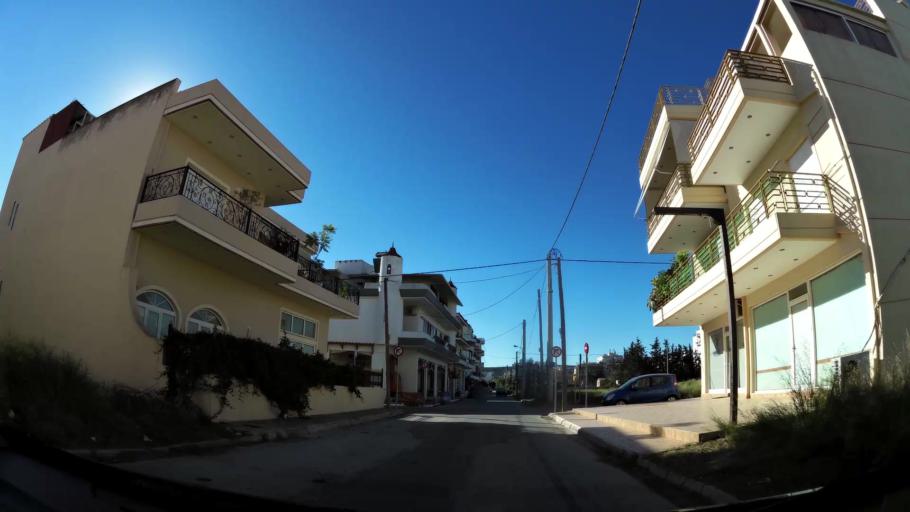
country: GR
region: Attica
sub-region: Nomarchia Anatolikis Attikis
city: Koropi
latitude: 37.9097
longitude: 23.8701
